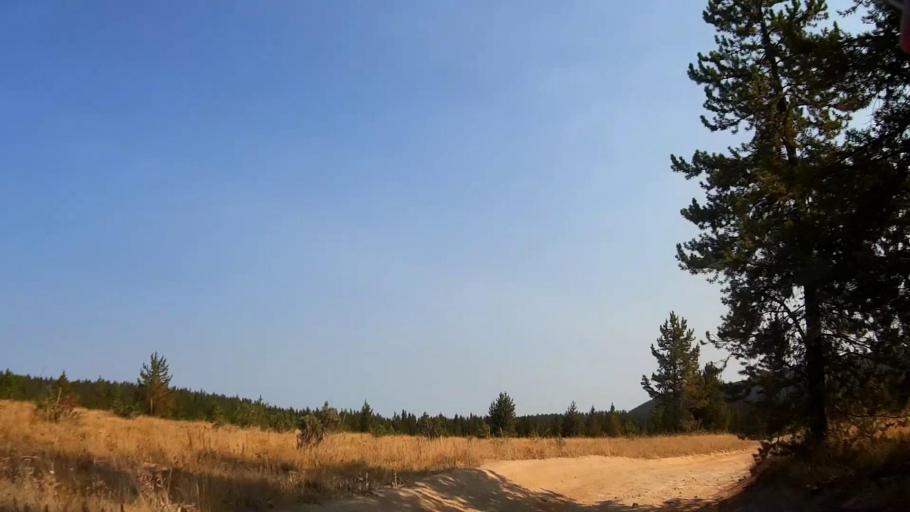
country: US
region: Montana
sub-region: Gallatin County
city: West Yellowstone
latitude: 44.5735
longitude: -111.1867
